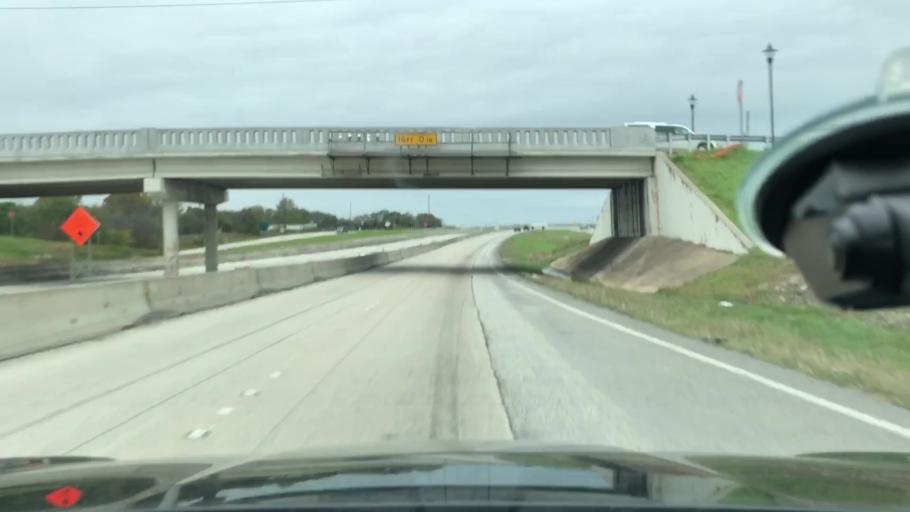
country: US
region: Texas
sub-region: Ellis County
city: Waxahachie
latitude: 32.3742
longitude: -96.8634
